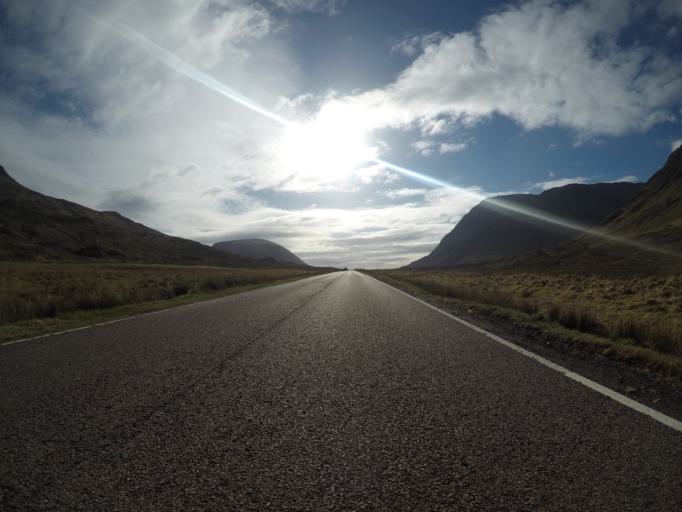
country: GB
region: Scotland
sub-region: Highland
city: Spean Bridge
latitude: 56.6638
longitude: -4.9386
